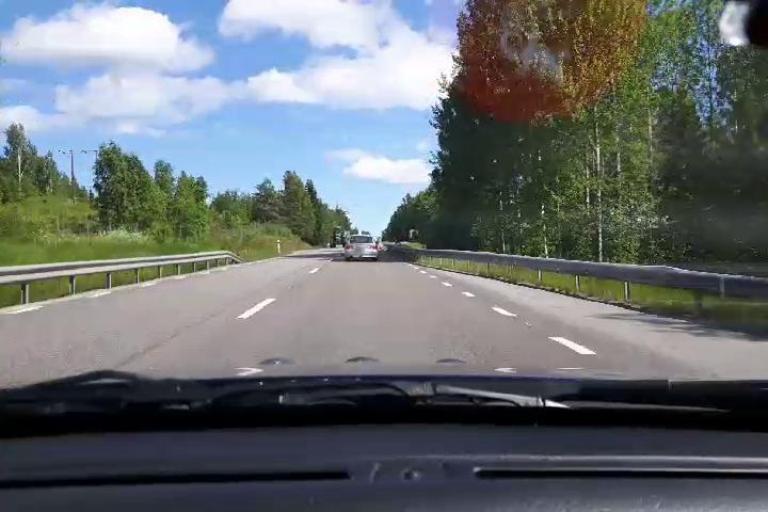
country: SE
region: Gaevleborg
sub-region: Hudiksvalls Kommun
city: Sorforsa
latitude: 61.7358
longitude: 16.9278
